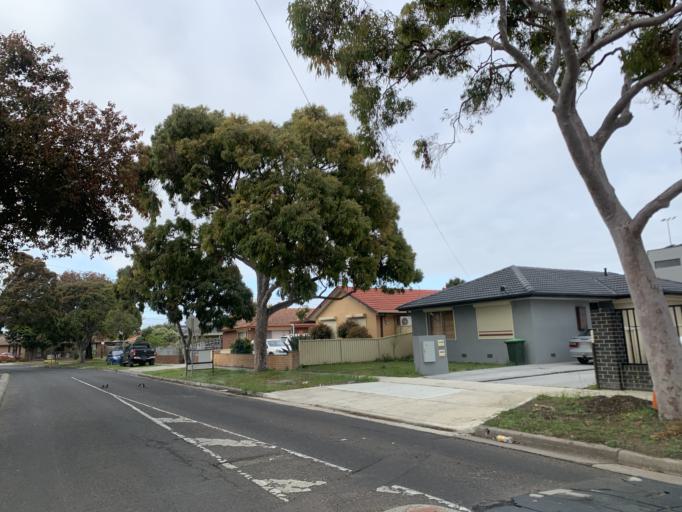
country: AU
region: Victoria
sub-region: Brimbank
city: Kealba
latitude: -37.7492
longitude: 144.8209
